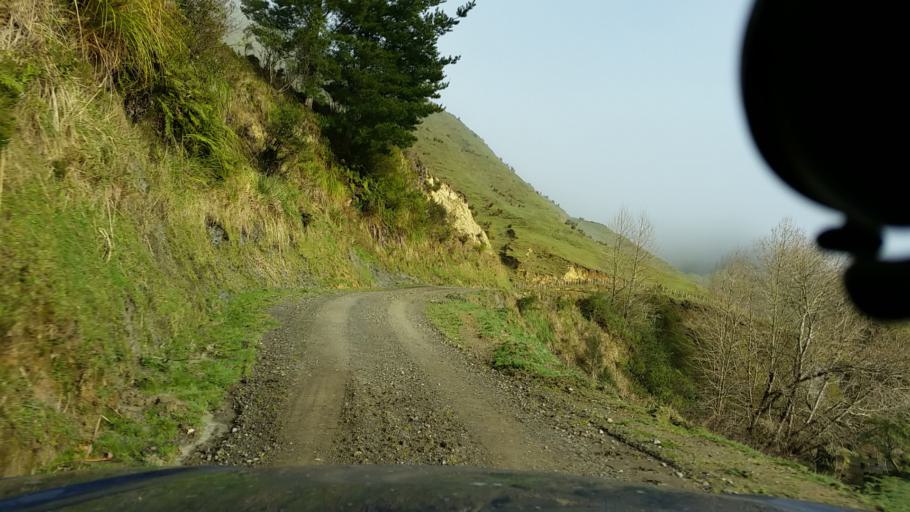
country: NZ
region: Taranaki
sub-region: New Plymouth District
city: Waitara
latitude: -38.9781
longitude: 174.7498
